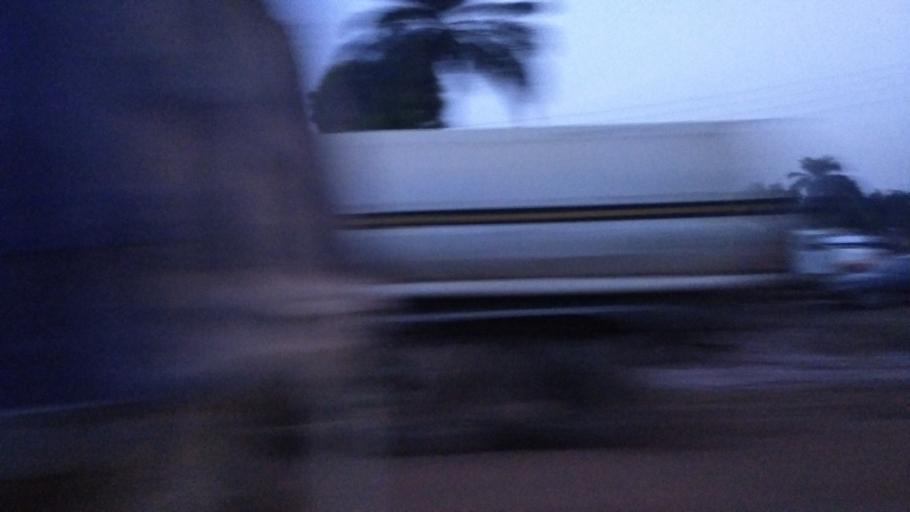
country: NG
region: Enugu
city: Enugu
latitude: 6.4658
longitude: 7.5947
